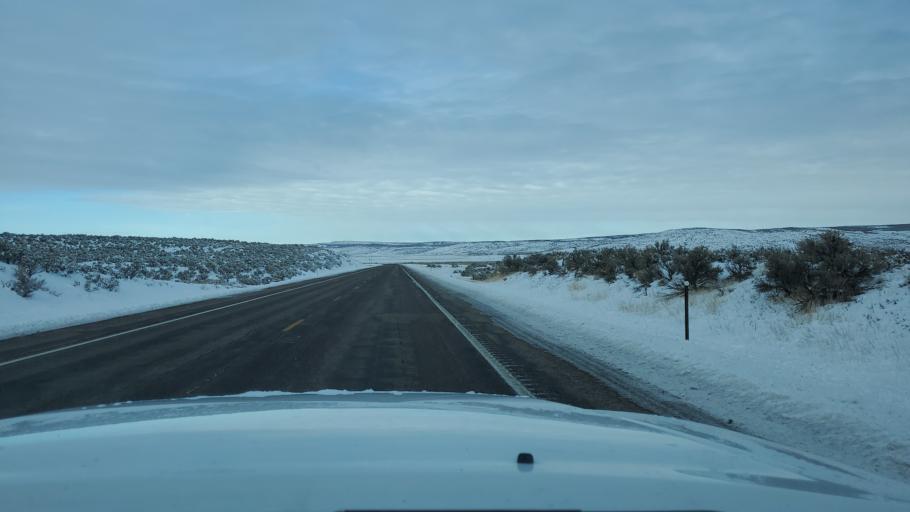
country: US
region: Colorado
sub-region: Moffat County
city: Craig
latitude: 40.5305
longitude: -107.7768
